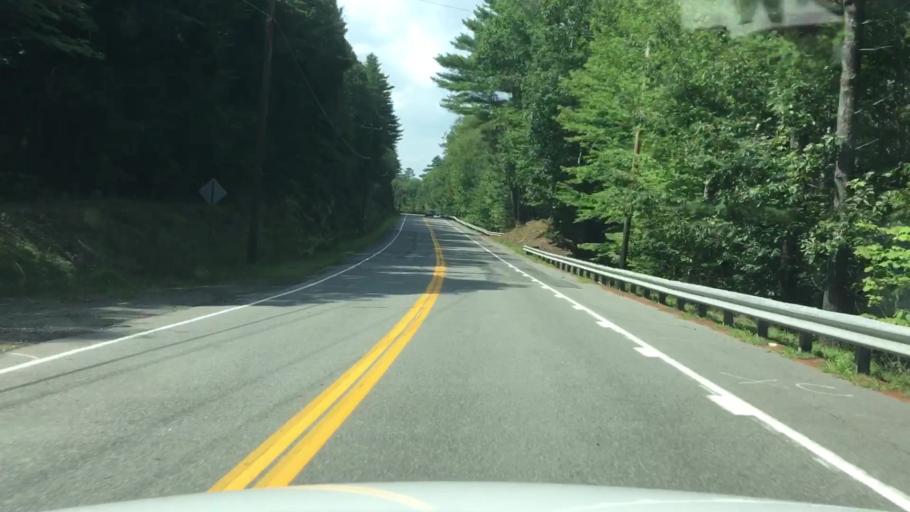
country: US
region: Maine
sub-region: Oxford County
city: Dixfield
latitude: 44.5302
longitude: -70.4687
